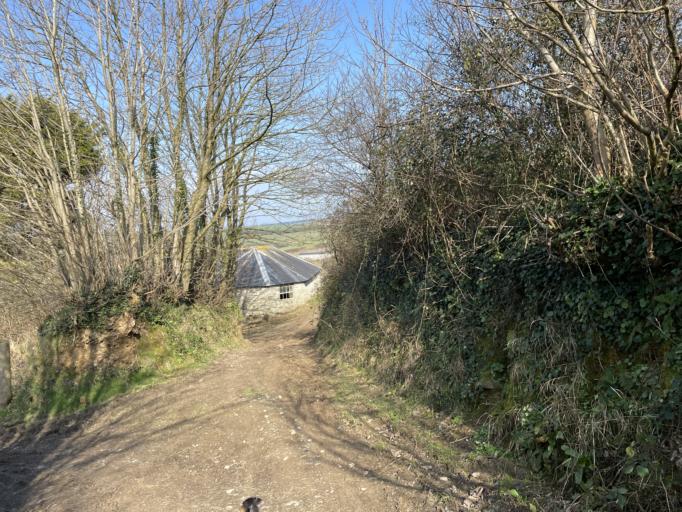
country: GB
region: England
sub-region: Devon
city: Braunton
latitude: 51.1281
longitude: -4.2057
